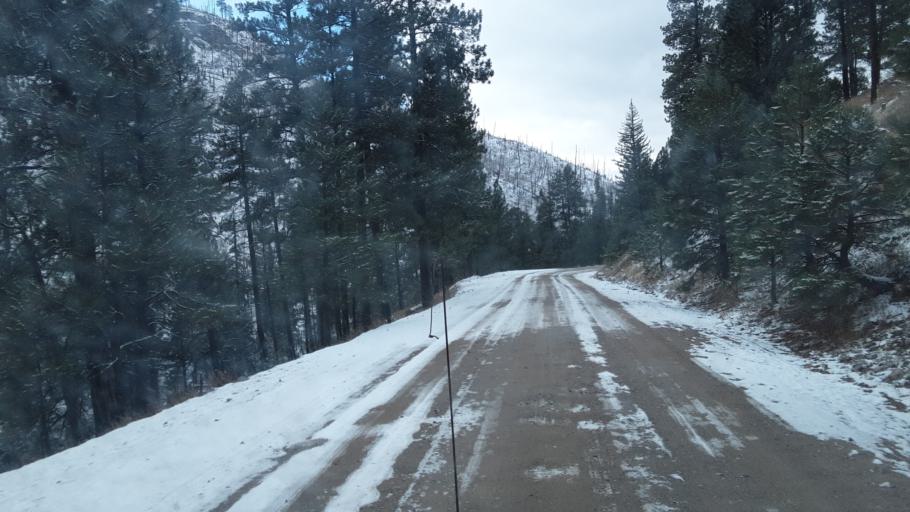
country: US
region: Colorado
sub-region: La Plata County
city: Bayfield
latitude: 37.4084
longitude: -107.5220
